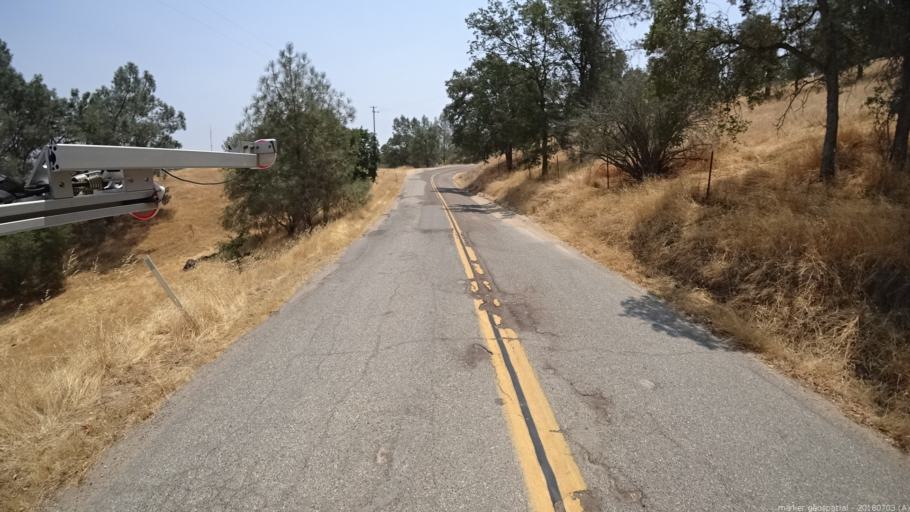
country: US
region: California
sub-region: Madera County
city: Yosemite Lakes
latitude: 37.0651
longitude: -119.6702
